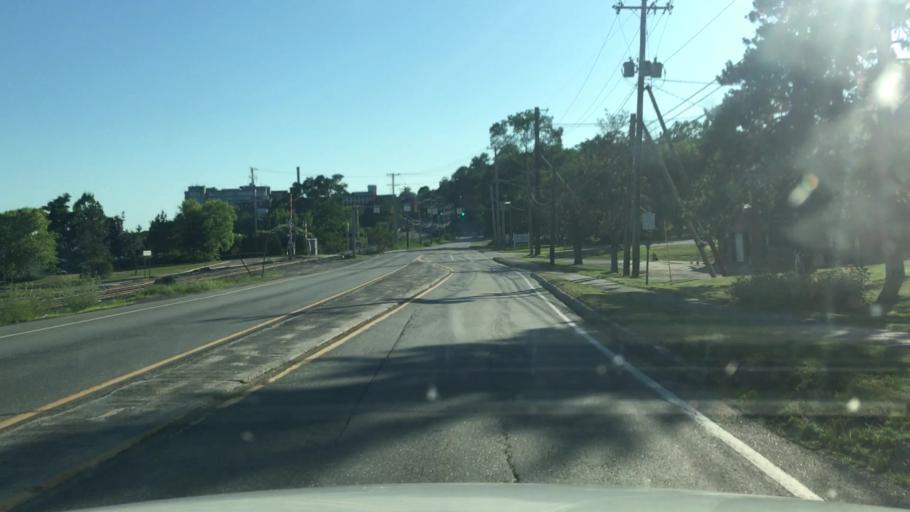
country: US
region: Maine
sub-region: Penobscot County
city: Brewer
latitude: 44.8120
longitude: -68.7423
